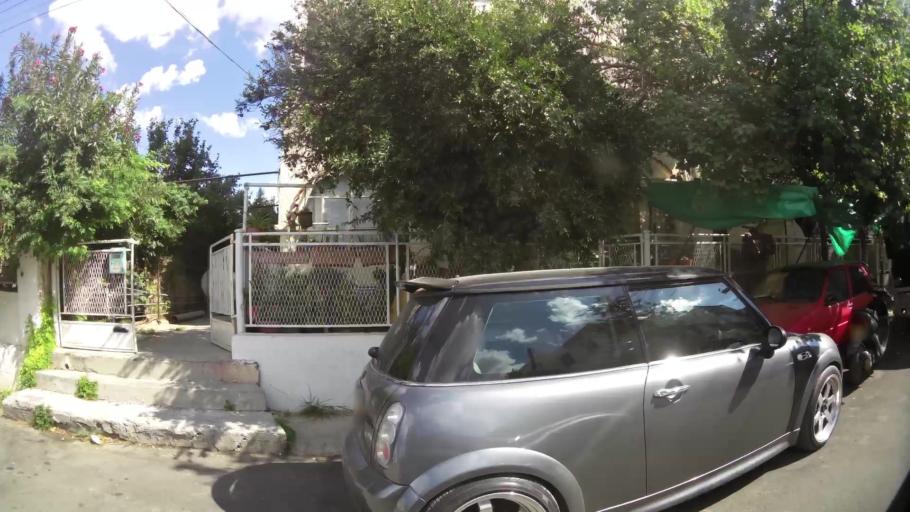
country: CY
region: Lefkosia
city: Nicosia
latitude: 35.1837
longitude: 33.3684
